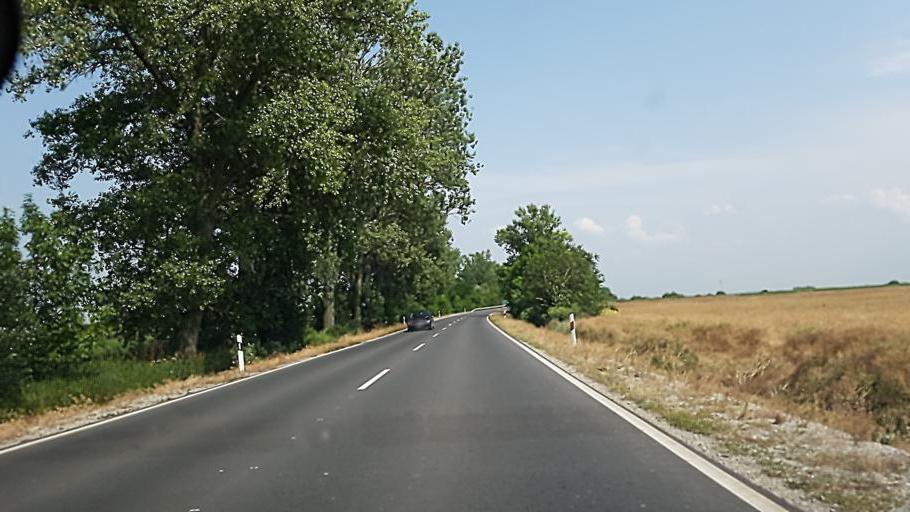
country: HU
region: Heves
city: Tiszanana
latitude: 47.6702
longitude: 20.5561
